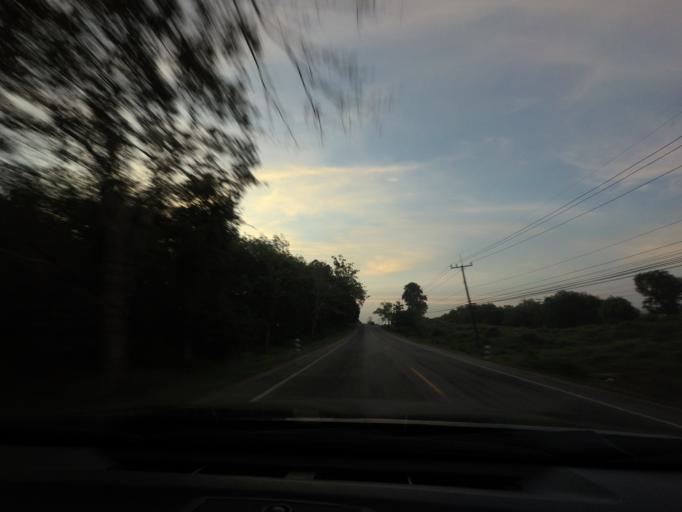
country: TH
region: Narathiwat
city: Rueso
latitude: 6.3725
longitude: 101.5305
